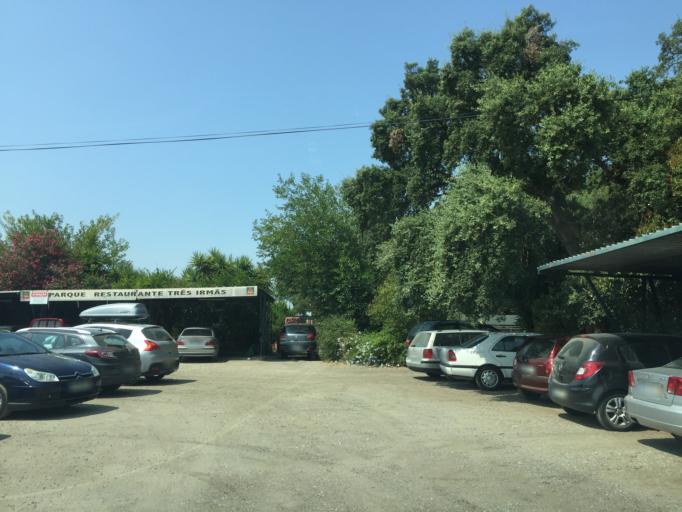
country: PT
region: Setubal
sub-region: Grandola
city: Grandola
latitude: 38.2148
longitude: -8.5594
